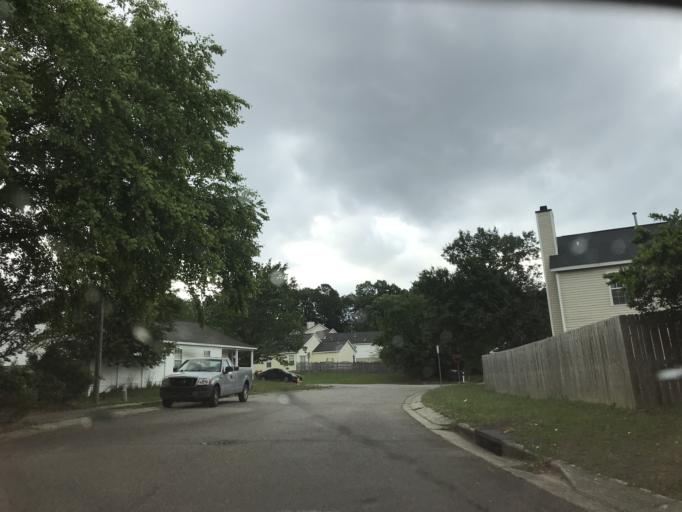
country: US
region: North Carolina
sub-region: Wake County
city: Knightdale
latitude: 35.8470
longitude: -78.5556
